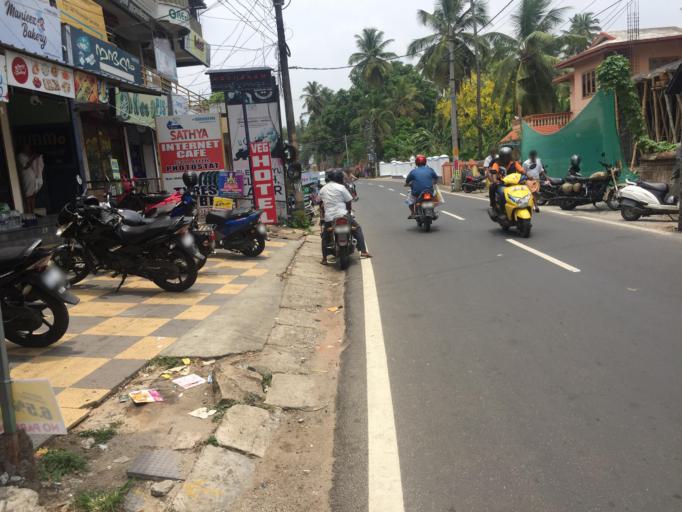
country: IN
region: Kerala
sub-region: Palakkad district
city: Chittur
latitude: 10.7011
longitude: 76.7395
